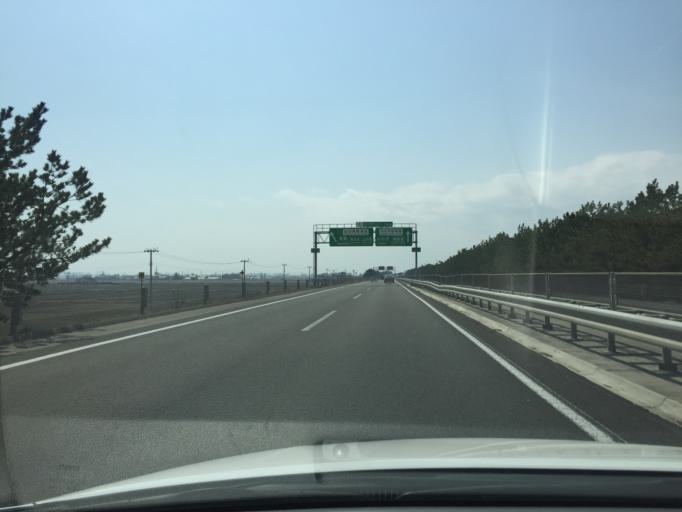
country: JP
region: Miyagi
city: Sendai
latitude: 38.2204
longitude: 140.9500
